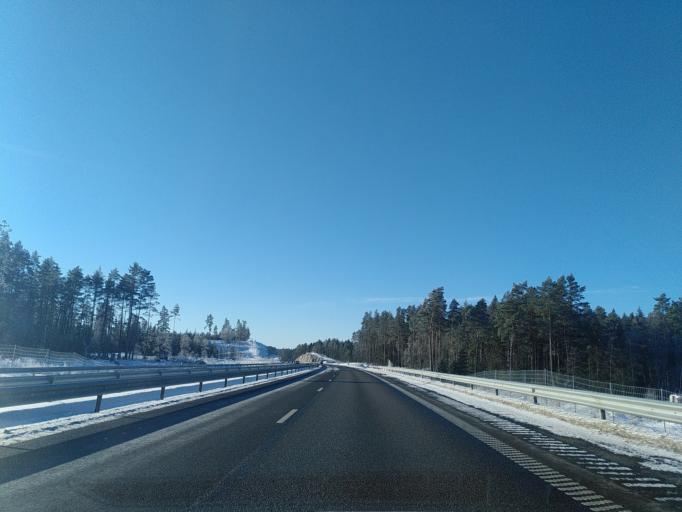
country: SE
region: Vaestra Goetaland
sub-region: Vargarda Kommun
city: Jonstorp
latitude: 57.9894
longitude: 12.7237
